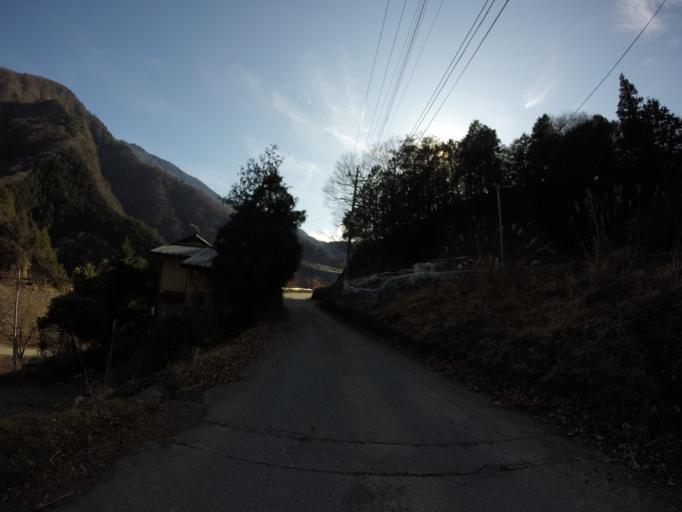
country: JP
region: Yamanashi
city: Ryuo
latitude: 35.3993
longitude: 138.3246
